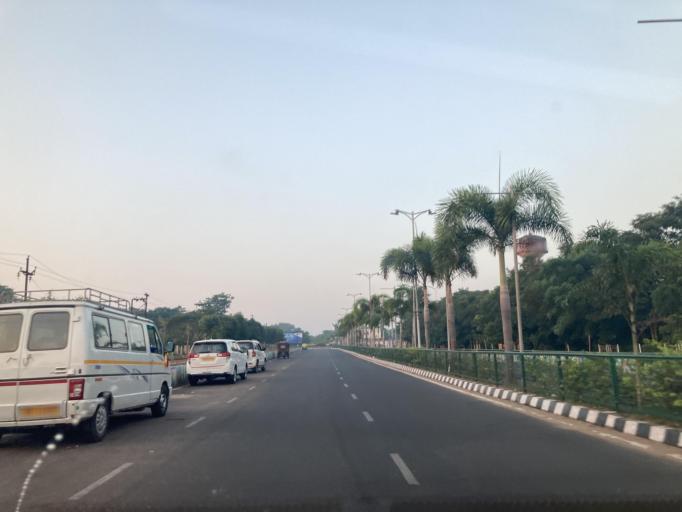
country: IN
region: Odisha
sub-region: Khordha
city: Bhubaneshwar
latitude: 20.2551
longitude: 85.8212
